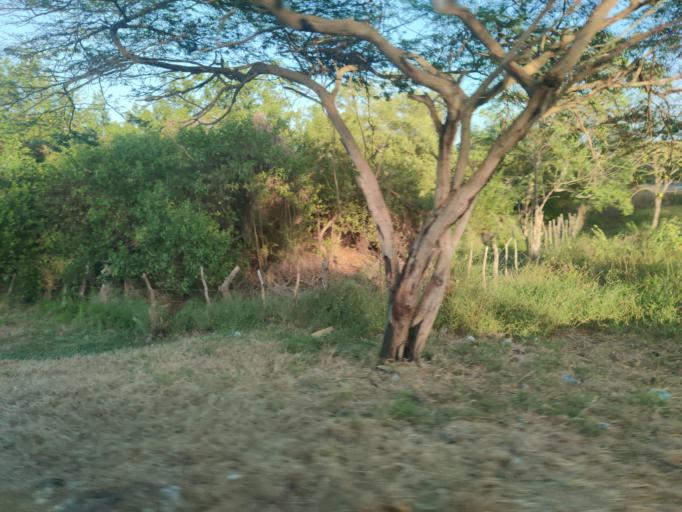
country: CO
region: Atlantico
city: Piojo
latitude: 10.7493
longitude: -75.2500
